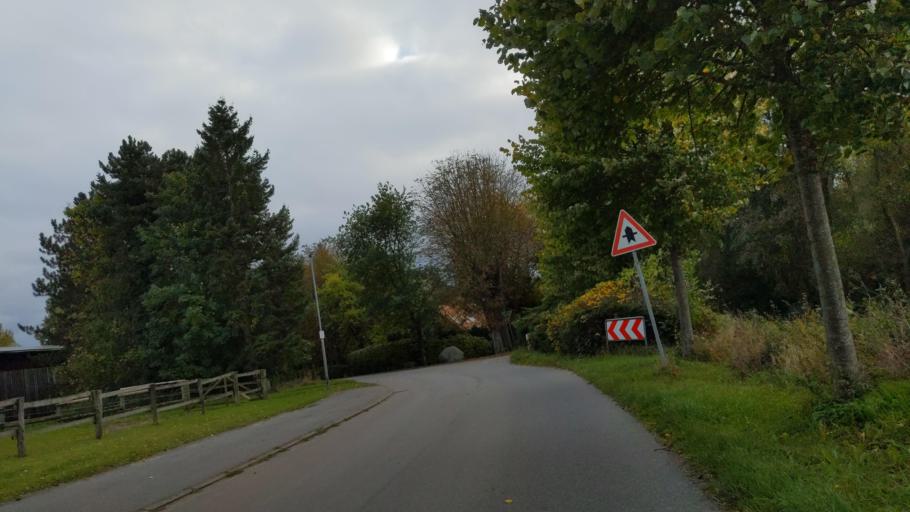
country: DE
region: Schleswig-Holstein
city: Sierksdorf
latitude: 54.0891
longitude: 10.7450
